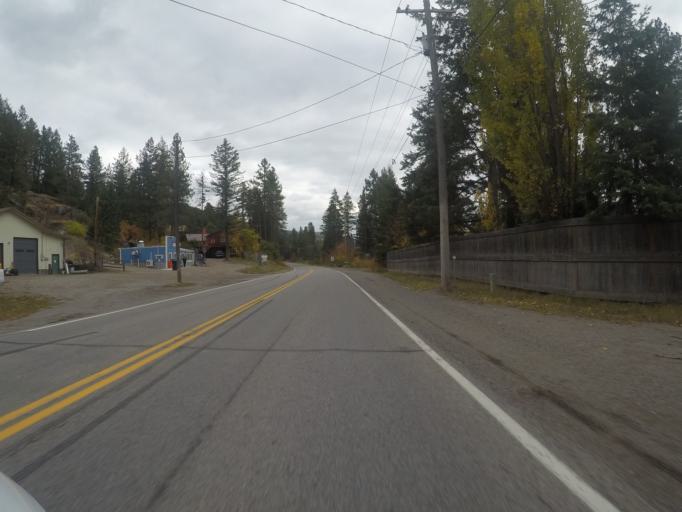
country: US
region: Montana
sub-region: Flathead County
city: Bigfork
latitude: 48.0023
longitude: -114.0508
